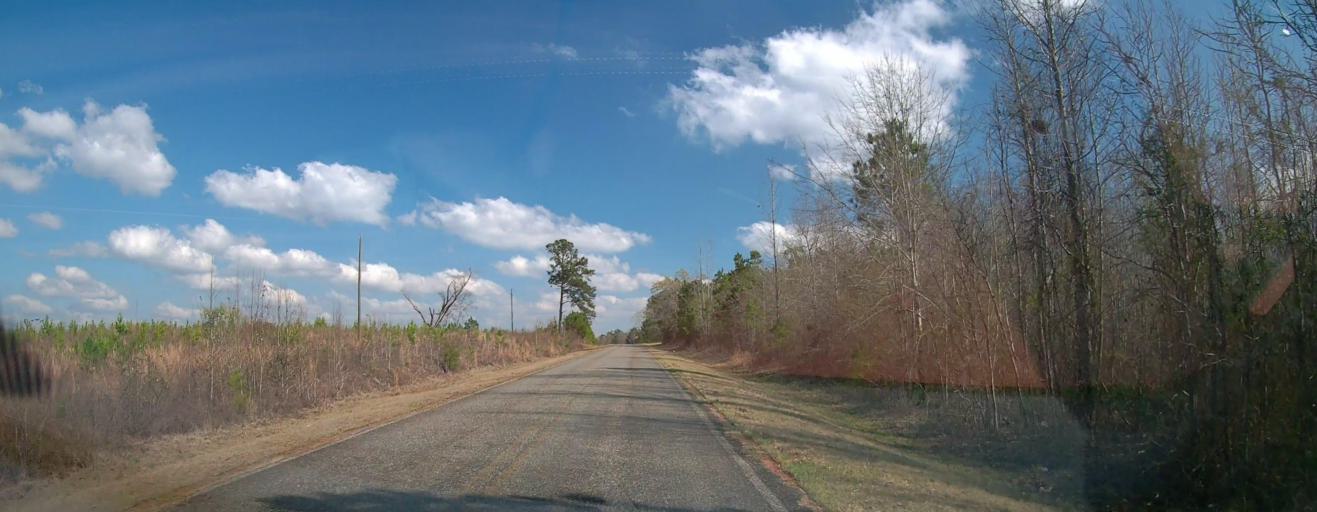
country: US
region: Georgia
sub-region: Twiggs County
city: Jeffersonville
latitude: 32.6446
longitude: -83.1893
